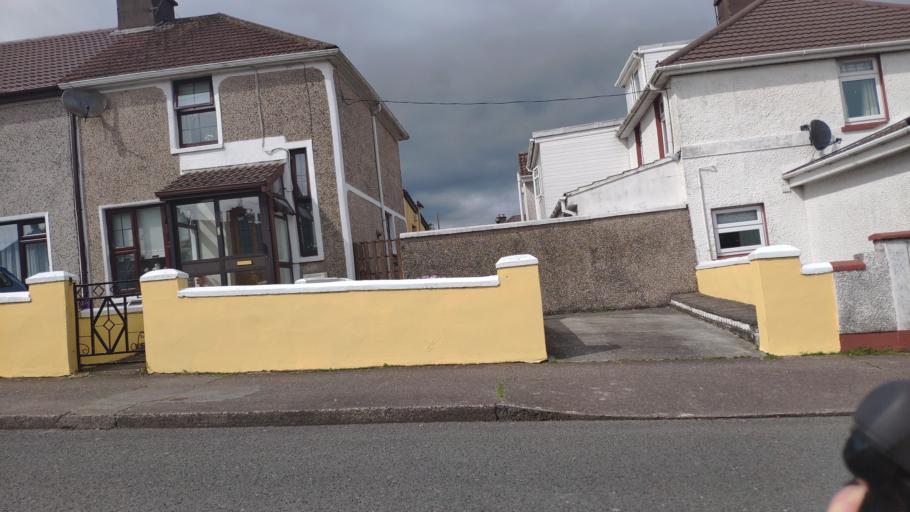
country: IE
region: Munster
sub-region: County Cork
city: Cork
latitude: 51.9048
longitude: -8.4840
